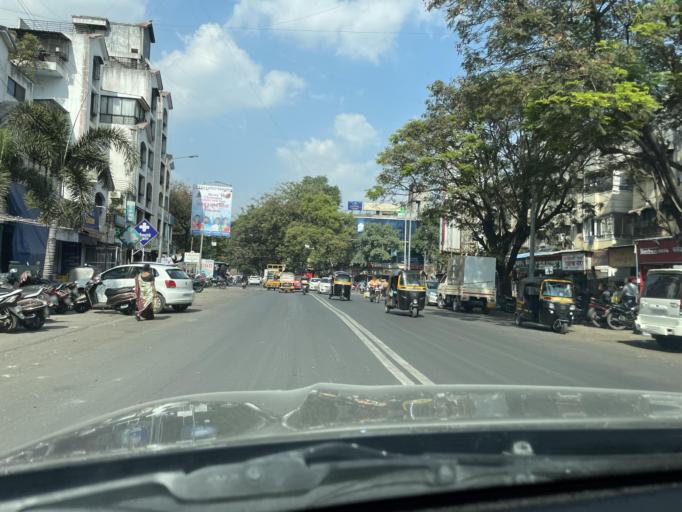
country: IN
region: Maharashtra
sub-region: Pune Division
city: Pune
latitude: 18.4943
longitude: 73.8999
